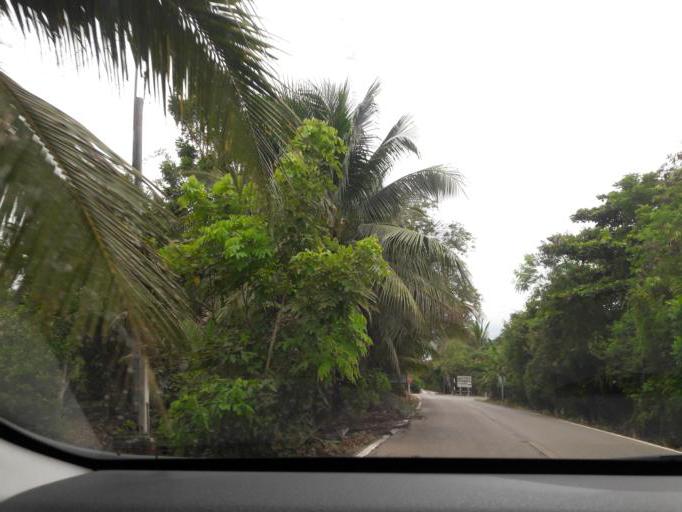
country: TH
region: Ratchaburi
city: Damnoen Saduak
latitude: 13.5636
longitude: 99.9791
